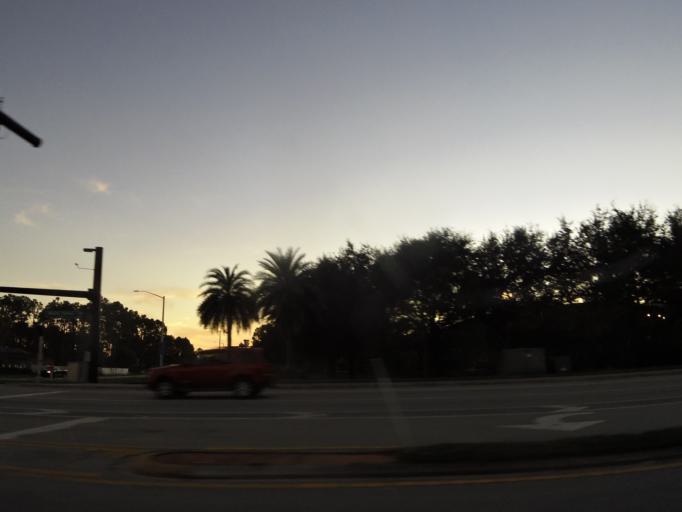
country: US
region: Florida
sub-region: Flagler County
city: Palm Coast
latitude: 29.5685
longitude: -81.2489
